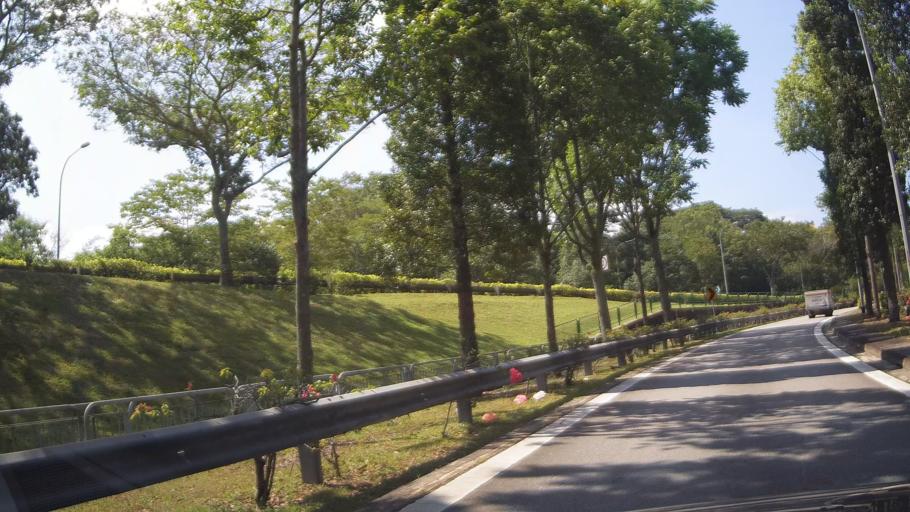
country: MY
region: Johor
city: Johor Bahru
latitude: 1.4219
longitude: 103.7726
